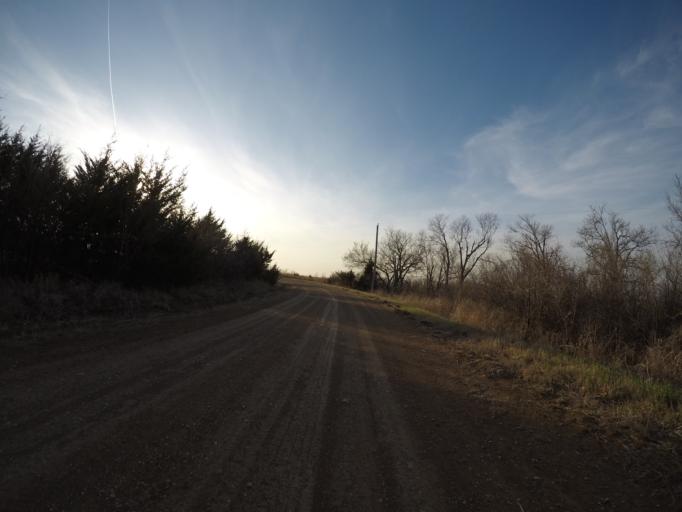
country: US
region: Kansas
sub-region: Riley County
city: Manhattan
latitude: 39.2542
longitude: -96.6590
